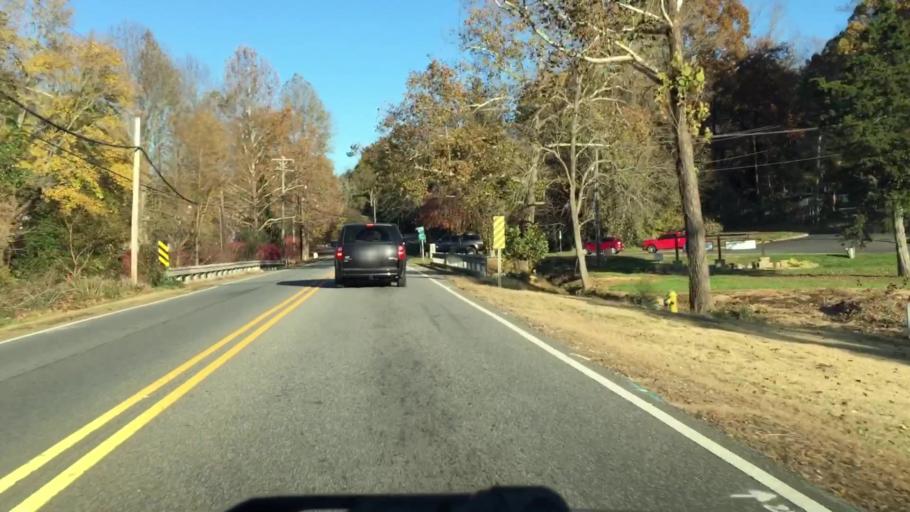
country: US
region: North Carolina
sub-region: Iredell County
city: Mooresville
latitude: 35.5799
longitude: -80.8333
